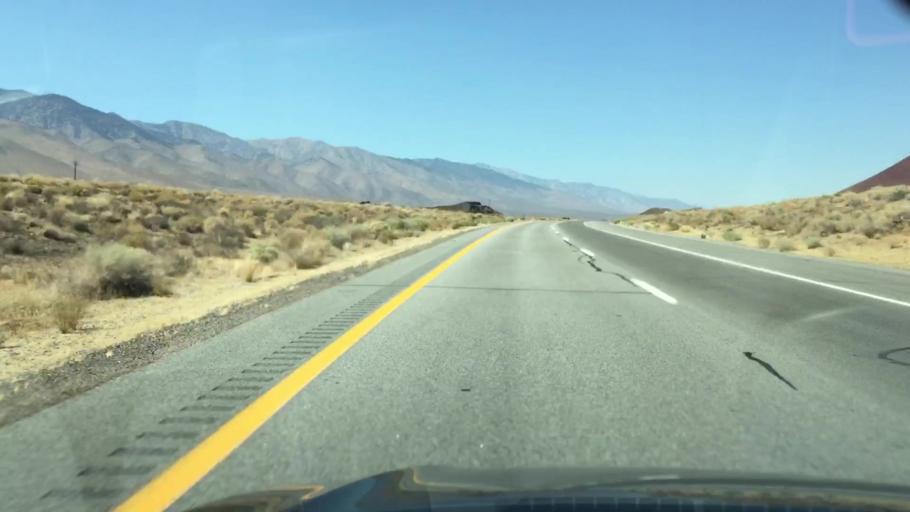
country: US
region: California
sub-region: Kern County
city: Inyokern
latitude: 35.9669
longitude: -117.9184
